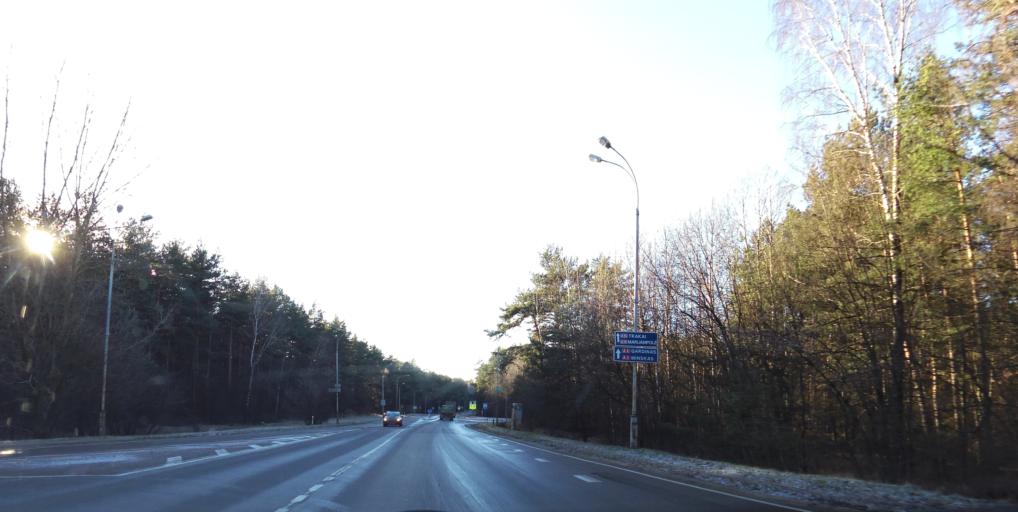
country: LT
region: Vilnius County
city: Lazdynai
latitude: 54.6403
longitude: 25.1803
